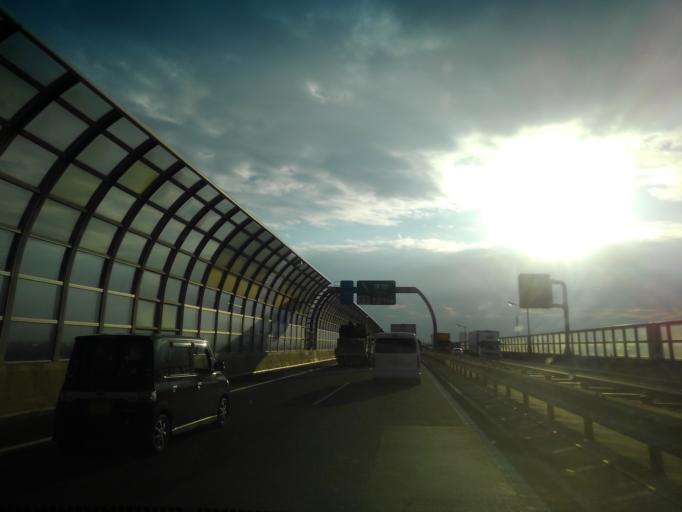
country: JP
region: Saitama
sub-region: Kawaguchi-shi
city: Hatogaya-honcho
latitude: 35.8491
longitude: 139.7675
